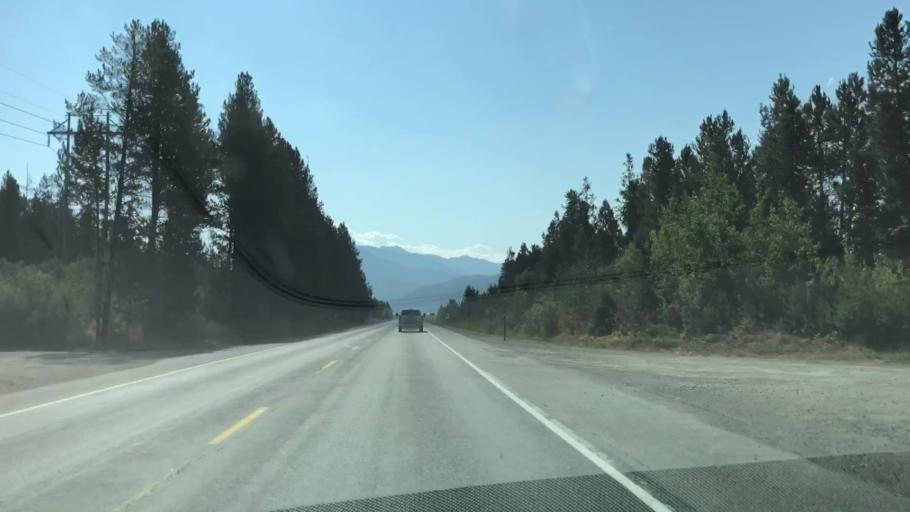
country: US
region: Wyoming
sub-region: Teton County
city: Hoback
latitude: 43.1972
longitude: -111.0410
